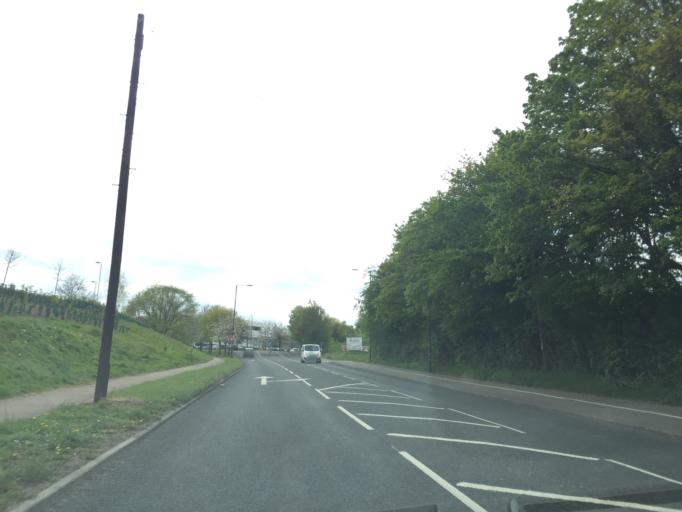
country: GB
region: England
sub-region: Essex
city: Roydon
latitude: 51.7712
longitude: 0.0701
